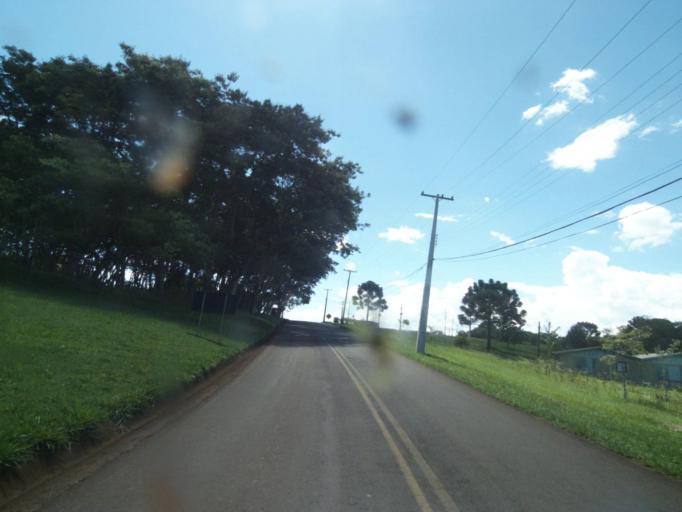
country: BR
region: Parana
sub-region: Pinhao
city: Pinhao
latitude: -25.7920
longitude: -52.0805
